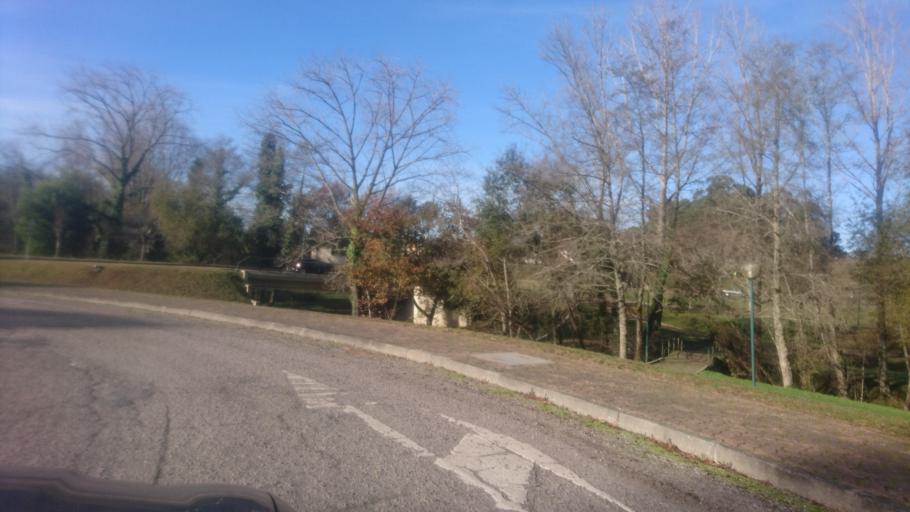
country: PT
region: Aveiro
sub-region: Santa Maria da Feira
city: Rio Meao
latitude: 40.9319
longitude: -8.5760
